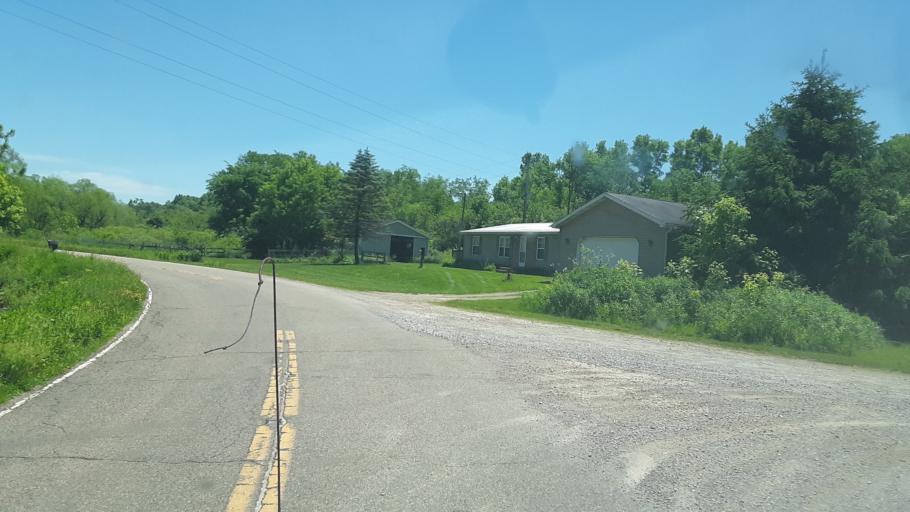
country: US
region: Ohio
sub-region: Coshocton County
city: Coshocton
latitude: 40.2906
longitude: -82.0072
